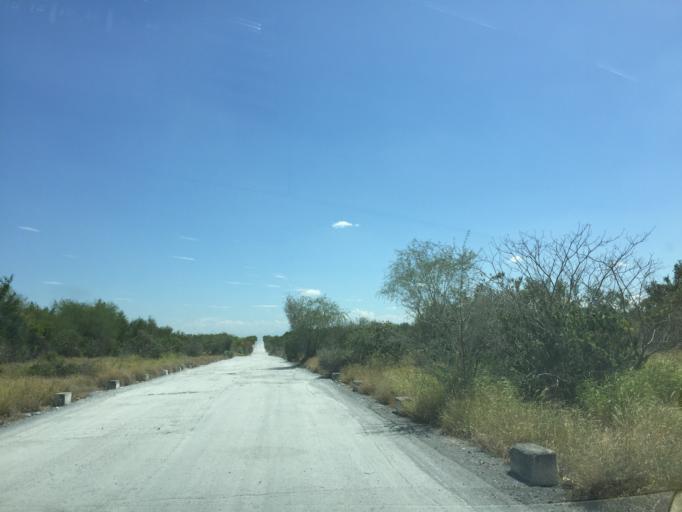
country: MX
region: Nuevo Leon
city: Marin
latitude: 25.8099
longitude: -99.8993
